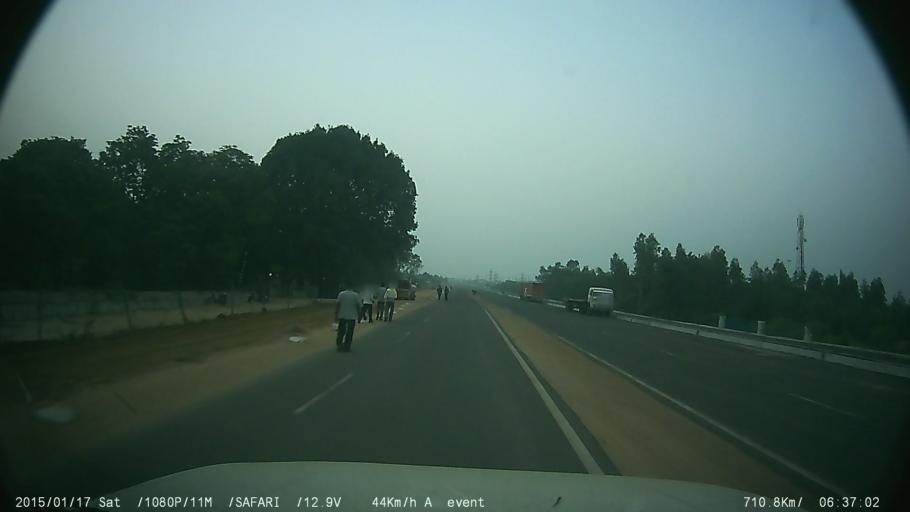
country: IN
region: Tamil Nadu
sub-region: Kancheepuram
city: Sriperumbudur
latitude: 12.9501
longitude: 79.9387
